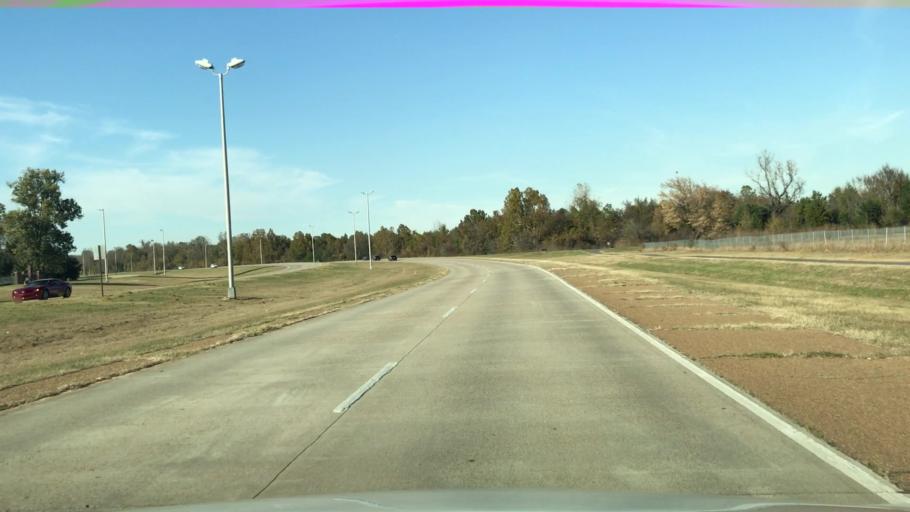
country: US
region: Louisiana
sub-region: Bossier Parish
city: Bossier City
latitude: 32.4822
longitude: -93.6932
